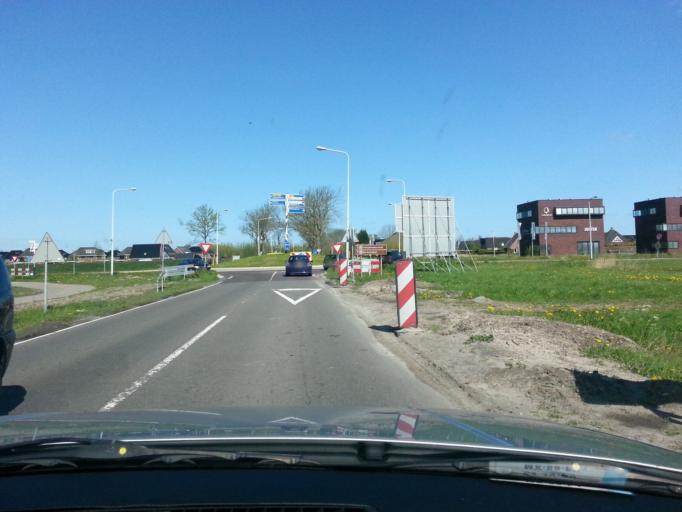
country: NL
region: Friesland
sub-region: Gemeente Achtkarspelen
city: Buitenpost
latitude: 53.2419
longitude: 6.1574
